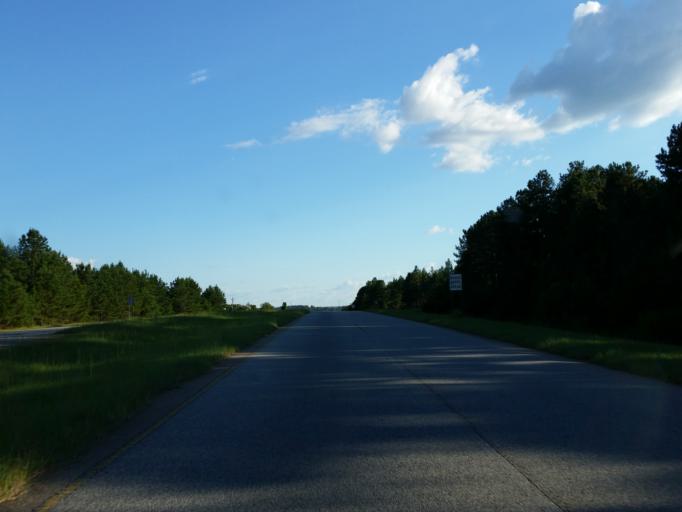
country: US
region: Georgia
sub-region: Houston County
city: Perry
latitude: 32.4694
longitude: -83.7782
